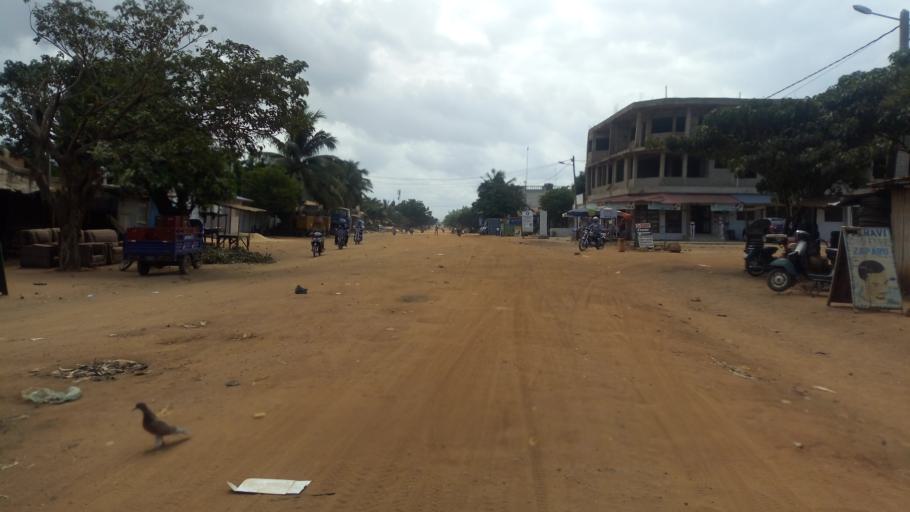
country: TG
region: Maritime
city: Lome
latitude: 6.2204
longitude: 1.1824
